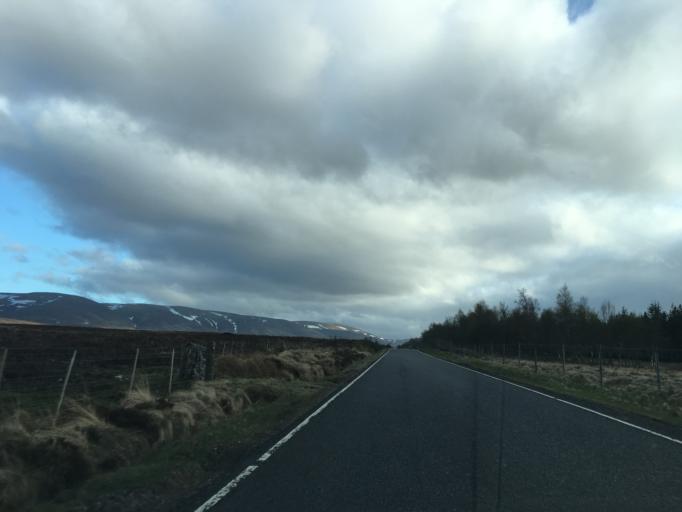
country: GB
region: Scotland
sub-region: Highland
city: Kingussie
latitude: 56.9540
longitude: -4.2443
